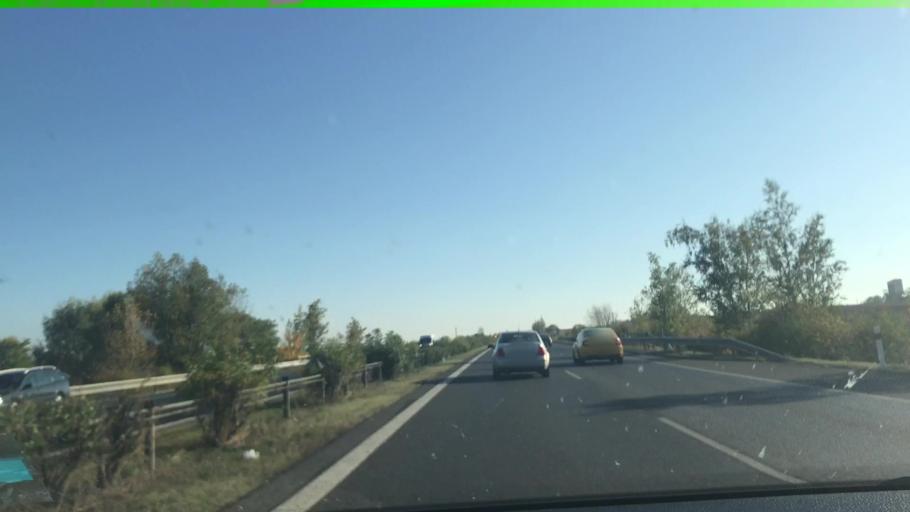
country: CZ
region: Ustecky
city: Roudnice nad Labem
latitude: 50.3486
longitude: 14.2774
